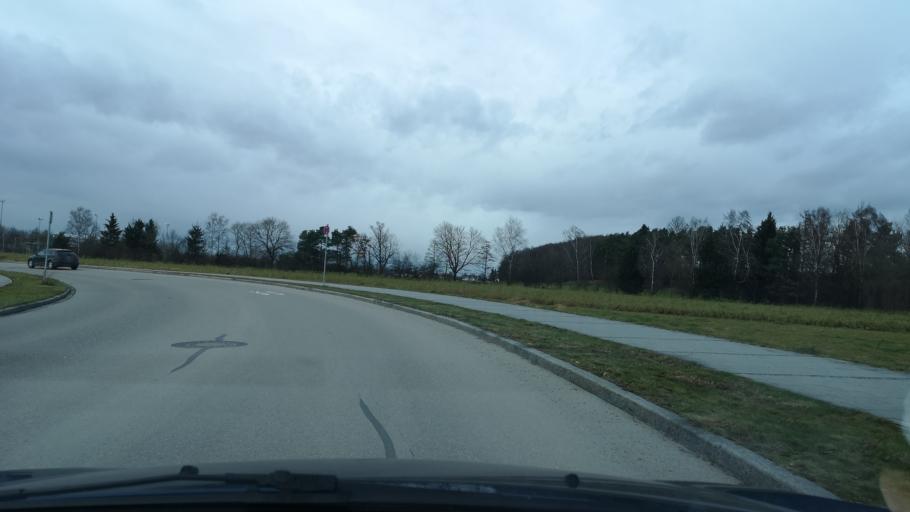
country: DE
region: Bavaria
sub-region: Upper Bavaria
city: Poing
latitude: 48.1741
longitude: 11.8170
